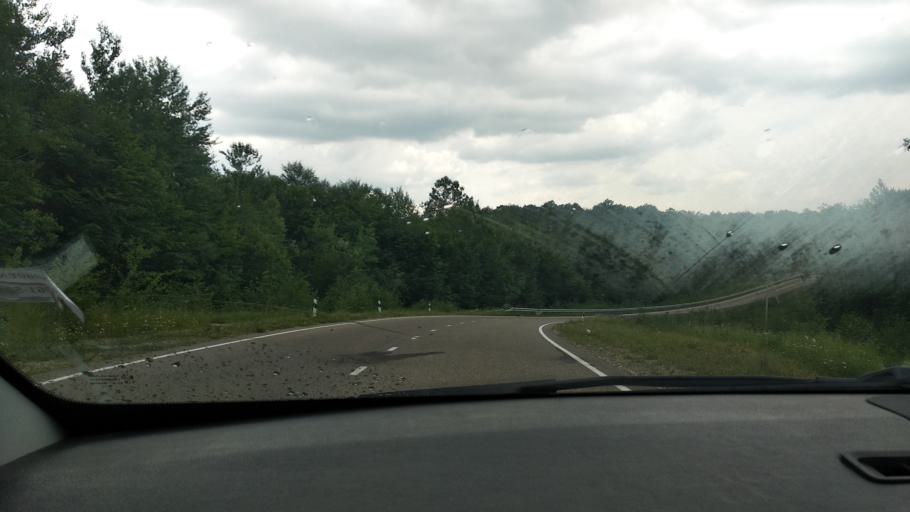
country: RU
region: Adygeya
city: Kamennomostskiy
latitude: 44.2688
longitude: 39.9432
